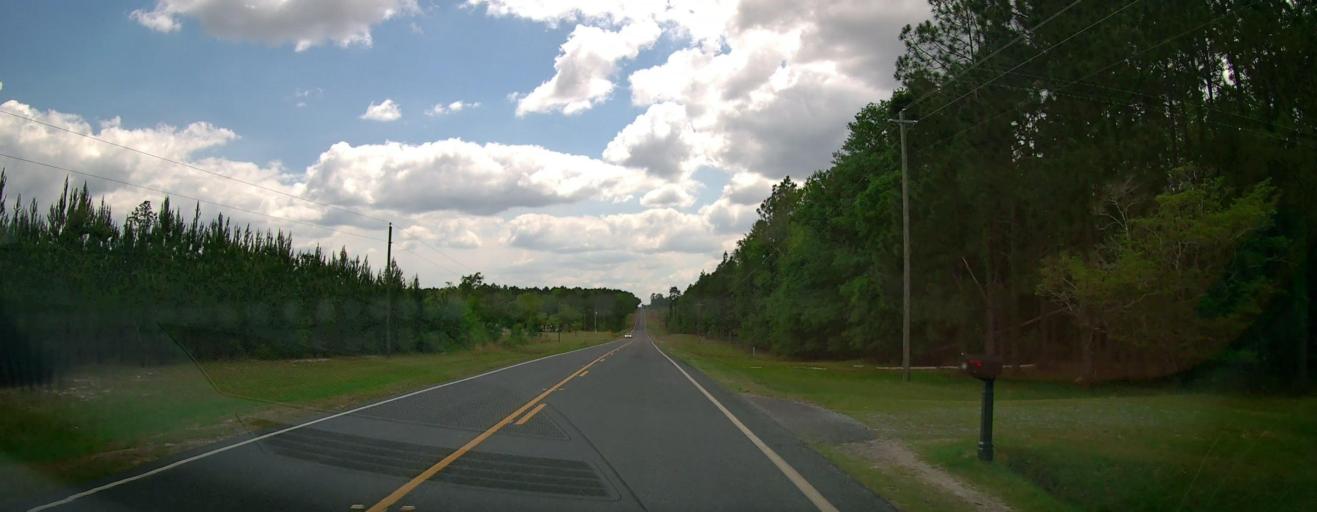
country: US
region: Georgia
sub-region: Treutlen County
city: Soperton
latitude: 32.4549
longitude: -82.6045
